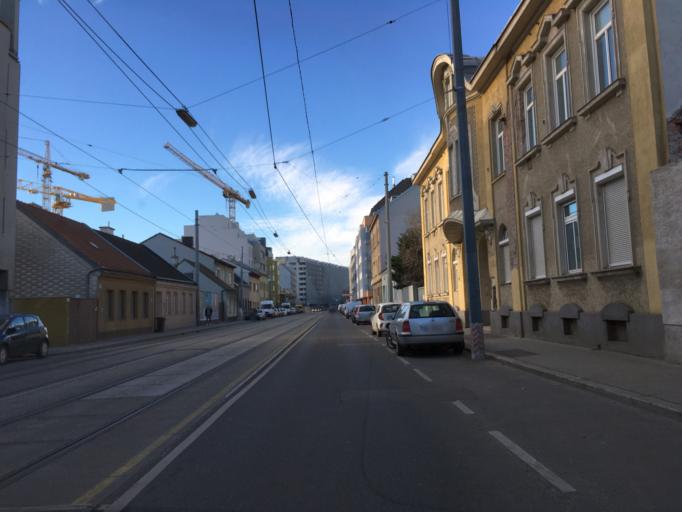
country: AT
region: Lower Austria
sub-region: Politischer Bezirk Wien-Umgebung
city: Gerasdorf bei Wien
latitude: 48.2508
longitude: 16.4344
